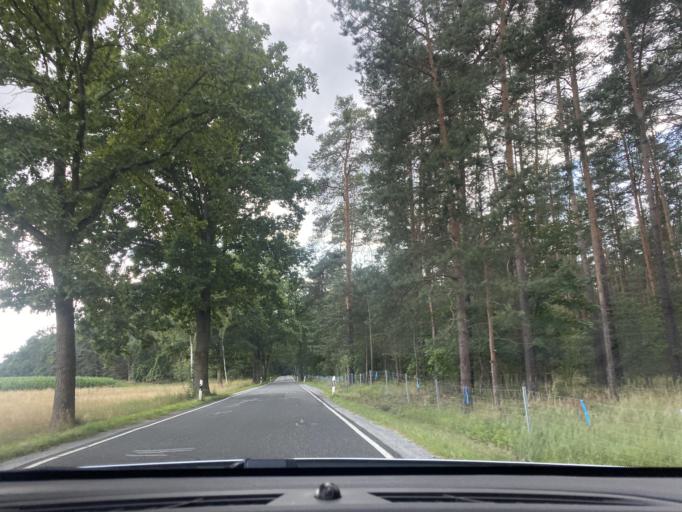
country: DE
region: Saxony
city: Klitten
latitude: 51.3693
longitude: 14.6097
